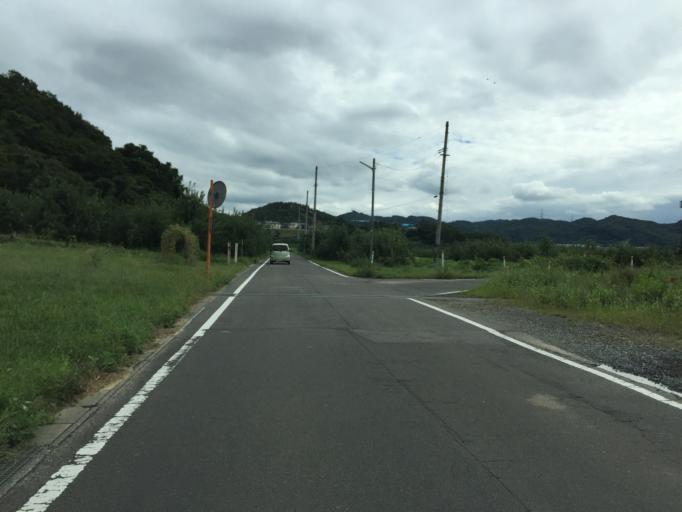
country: JP
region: Fukushima
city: Hobaramachi
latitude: 37.8013
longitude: 140.5098
